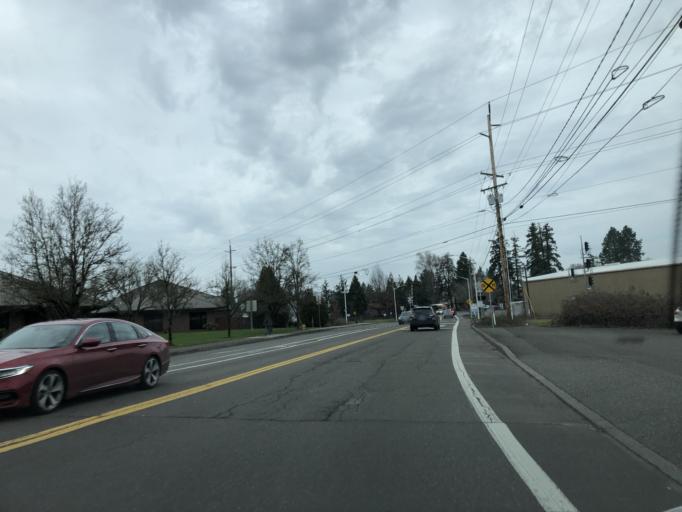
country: US
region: Oregon
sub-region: Washington County
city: Tigard
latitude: 45.4264
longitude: -122.7662
